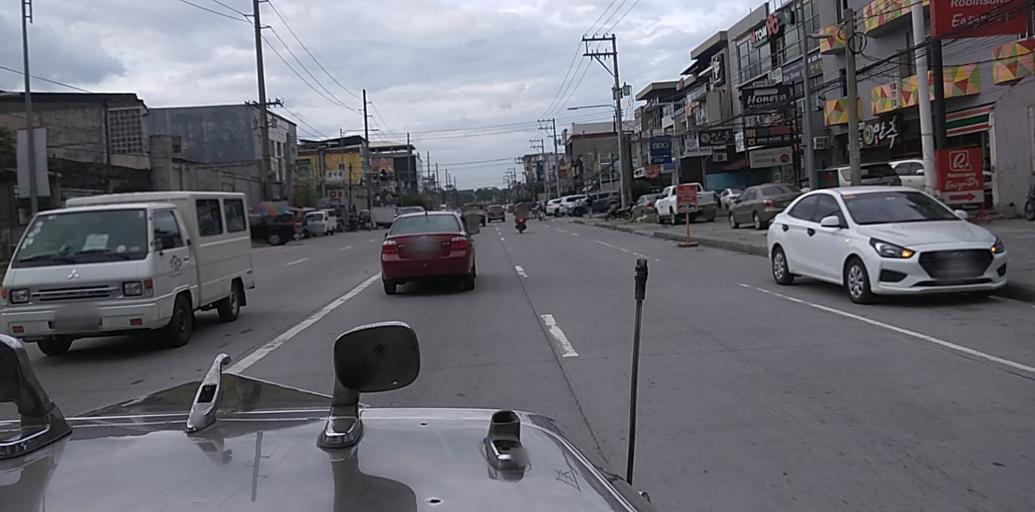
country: PH
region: Central Luzon
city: Santol
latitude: 15.1597
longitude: 120.5565
